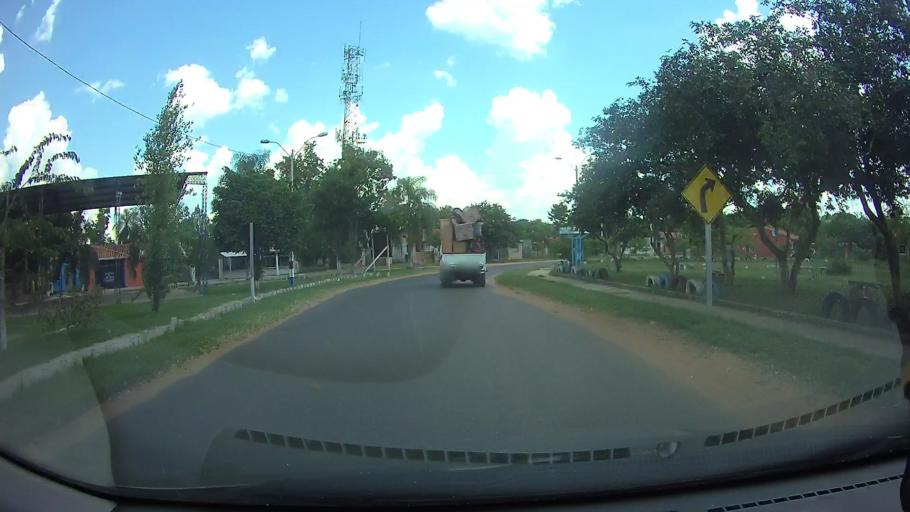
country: PY
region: Central
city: Limpio
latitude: -25.1667
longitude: -57.4343
